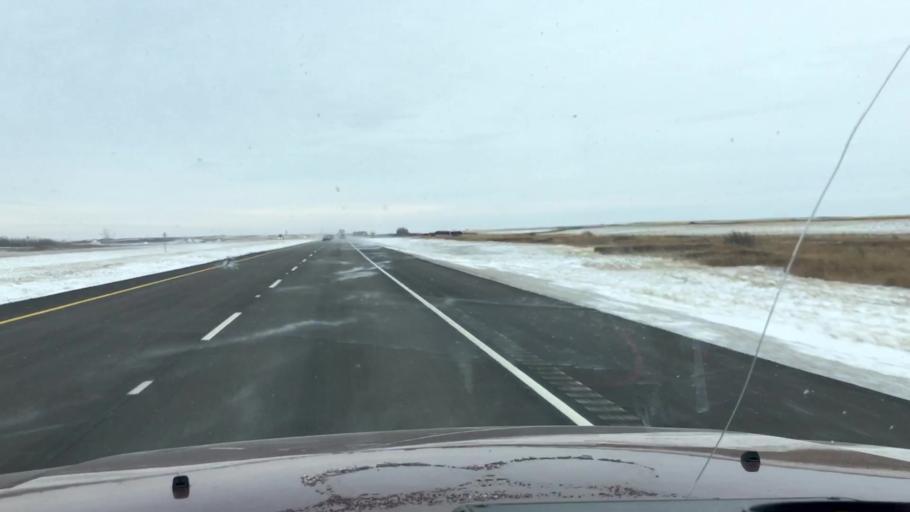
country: CA
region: Saskatchewan
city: Moose Jaw
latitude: 50.8957
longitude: -105.6297
